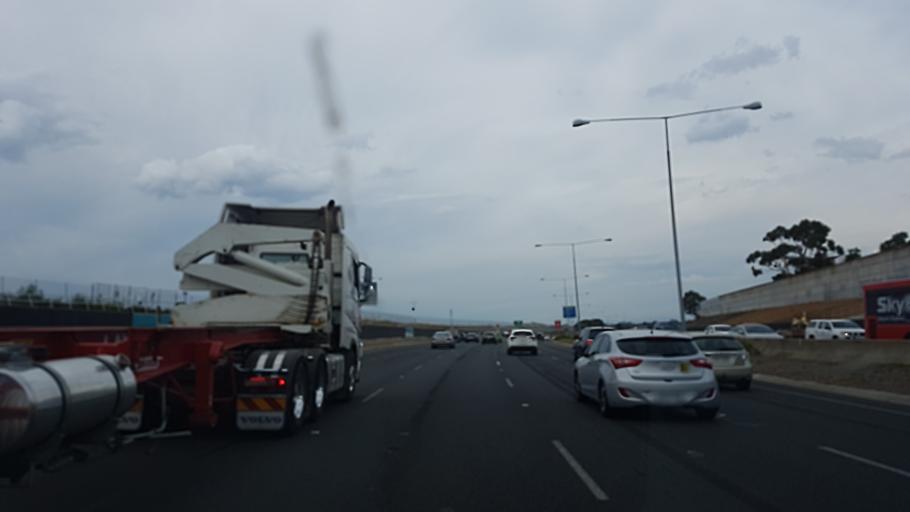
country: AU
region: Victoria
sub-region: Moonee Valley
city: Essendon North
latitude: -37.7330
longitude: 144.9110
